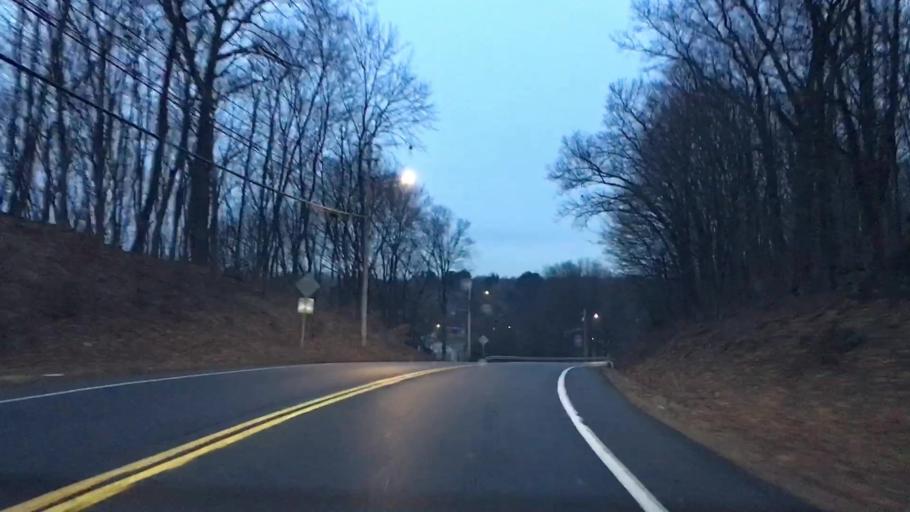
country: US
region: New York
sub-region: Dutchess County
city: Red Oaks Mill
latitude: 41.6721
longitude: -73.8848
